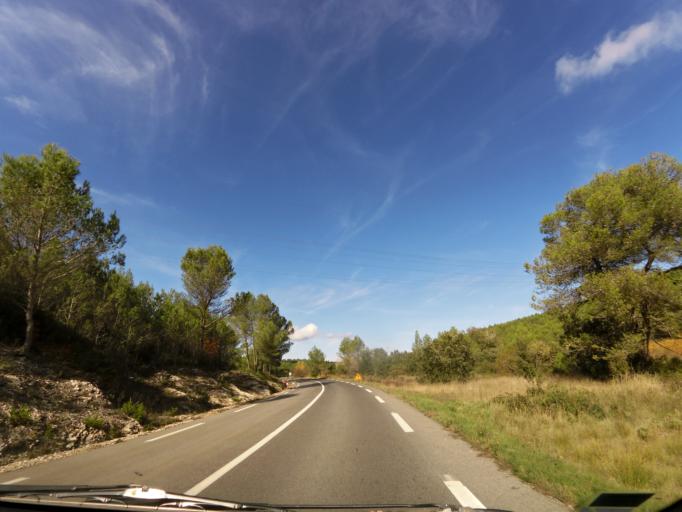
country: FR
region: Languedoc-Roussillon
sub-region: Departement du Gard
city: Villevieille
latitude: 43.8479
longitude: 4.0975
